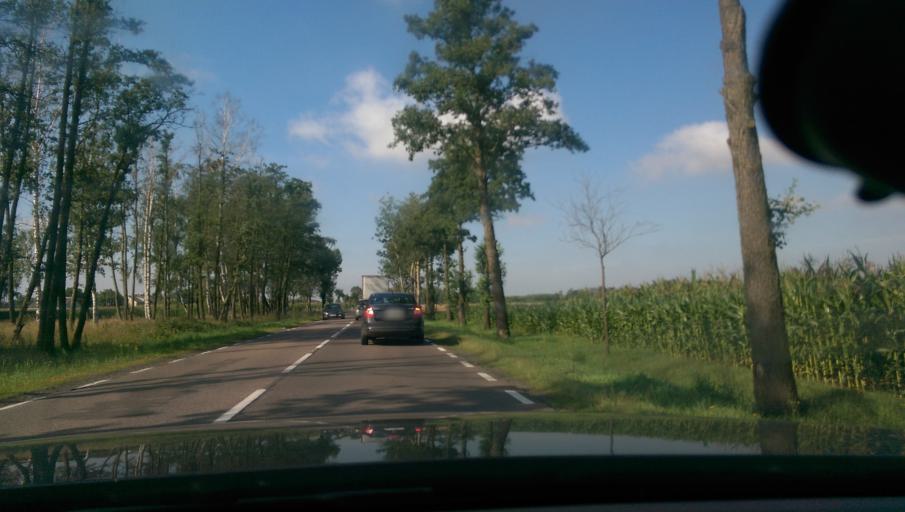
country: PL
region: Masovian Voivodeship
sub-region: Powiat plonski
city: Sochocin
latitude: 52.6588
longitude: 20.4372
